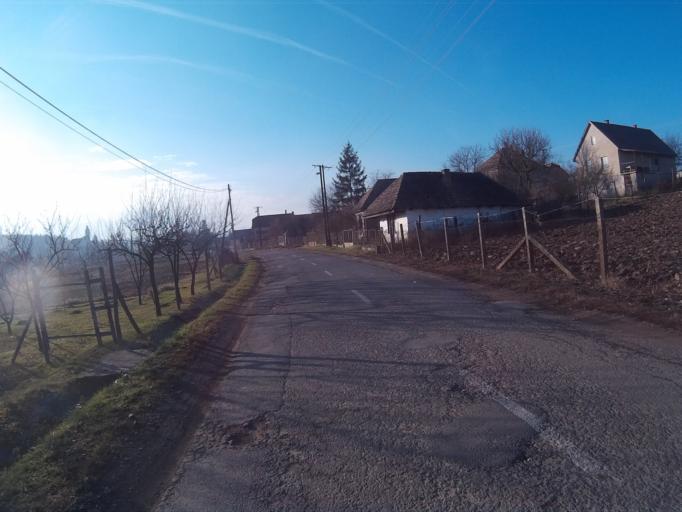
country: HU
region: Nograd
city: Bercel
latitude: 47.9765
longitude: 19.4300
